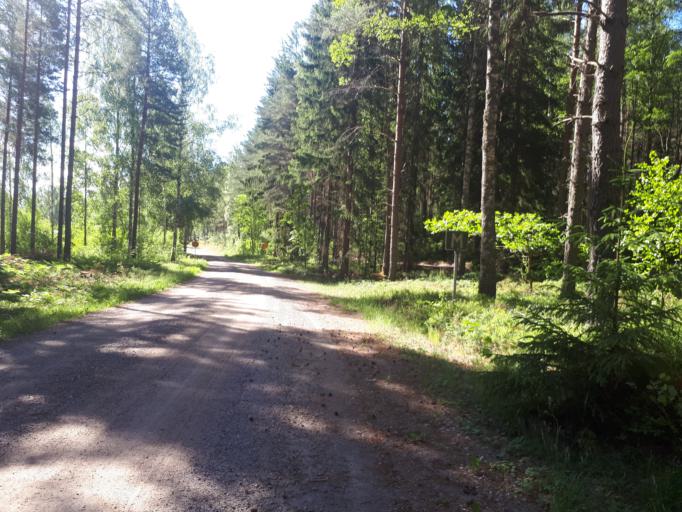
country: SE
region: Soedermanland
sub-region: Katrineholms Kommun
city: Katrineholm
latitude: 59.0958
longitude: 16.1985
